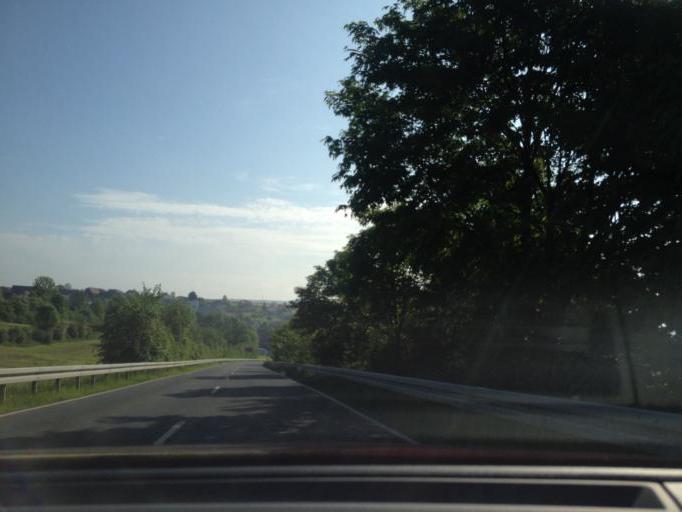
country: DE
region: Bavaria
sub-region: Upper Franconia
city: Pegnitz
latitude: 49.7639
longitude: 11.5960
